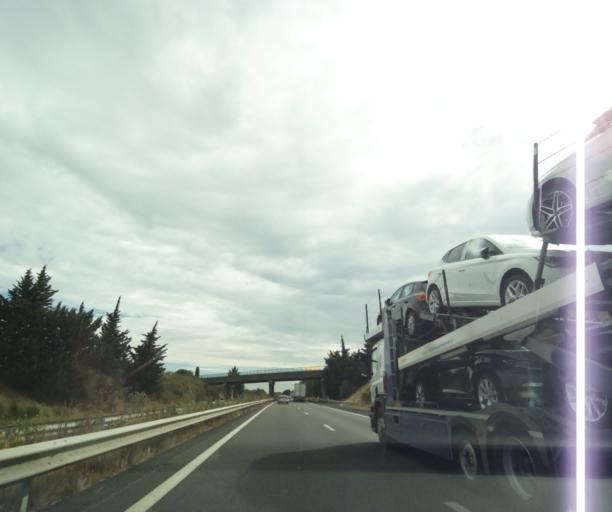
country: FR
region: Languedoc-Roussillon
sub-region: Departement du Gard
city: Garons
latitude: 43.7751
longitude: 4.4175
